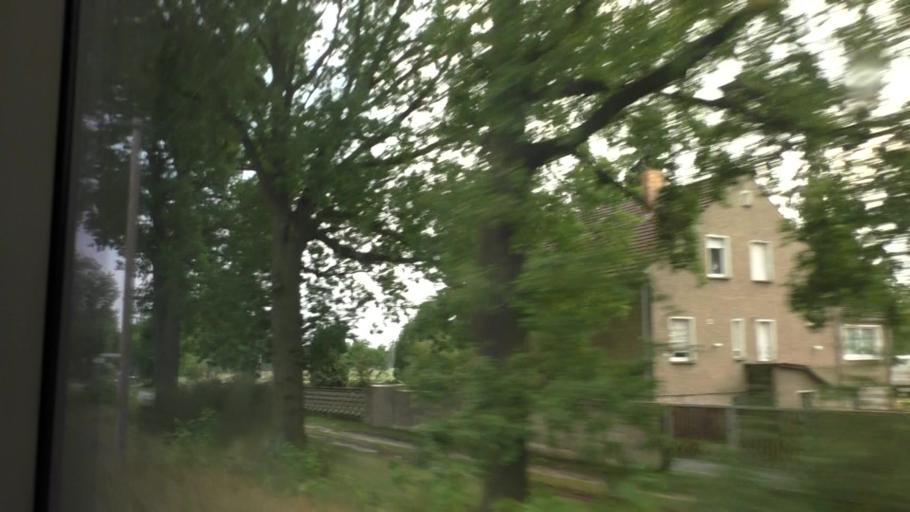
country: DE
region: Brandenburg
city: Storkow
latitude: 52.2759
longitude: 13.8723
